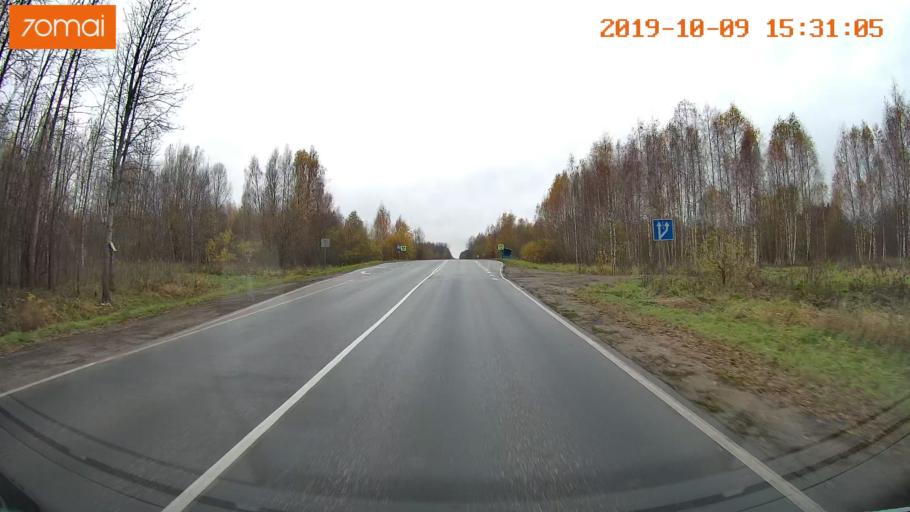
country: RU
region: Kostroma
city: Susanino
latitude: 57.9741
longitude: 41.3107
